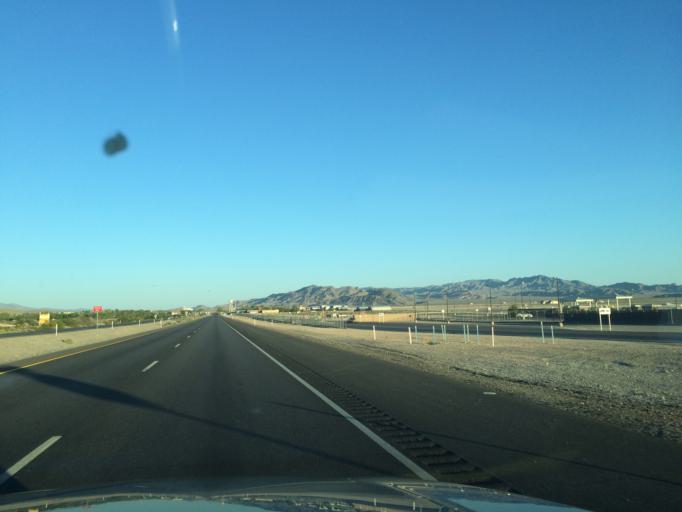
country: US
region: Nevada
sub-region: Nye County
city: Pahrump
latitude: 36.5773
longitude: -115.6561
